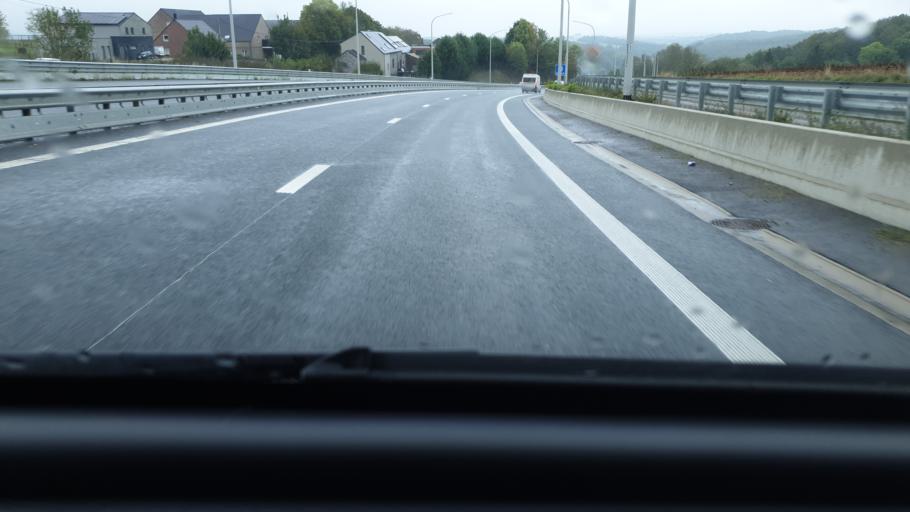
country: BE
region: Wallonia
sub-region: Province de Namur
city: Walcourt
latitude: 50.2696
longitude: 4.5021
